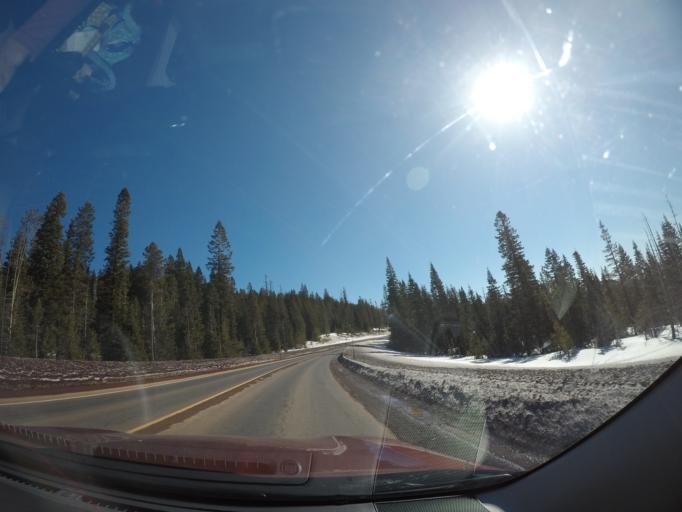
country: US
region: Oregon
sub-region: Deschutes County
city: Sunriver
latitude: 43.9827
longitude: -121.5926
